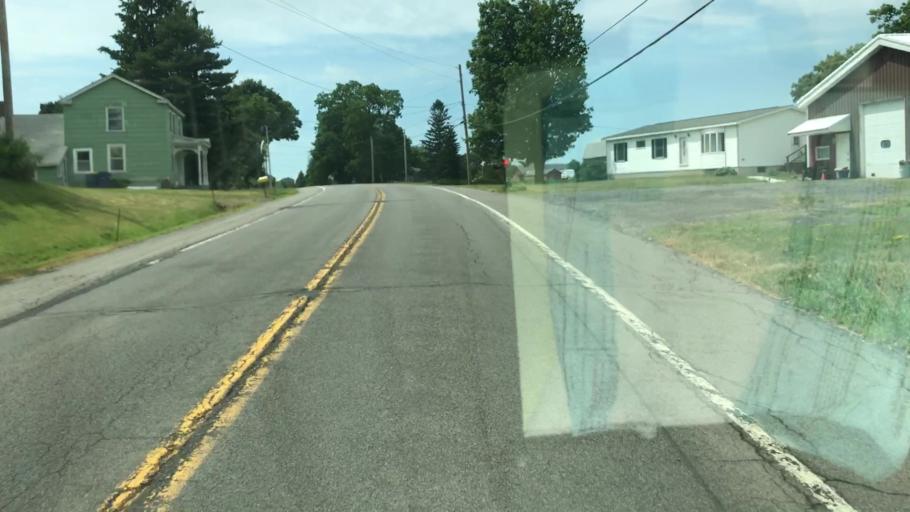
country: US
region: New York
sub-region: Onondaga County
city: Marcellus
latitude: 42.9328
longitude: -76.2909
